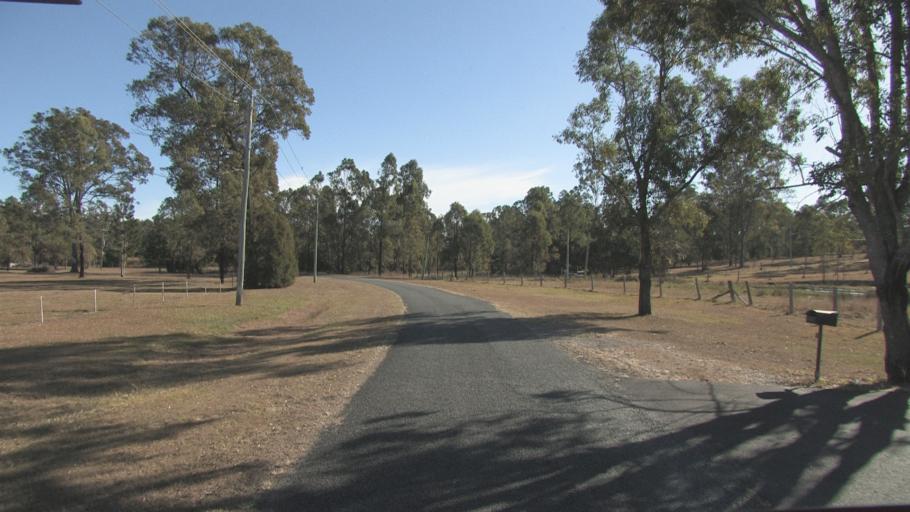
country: AU
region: Queensland
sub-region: Logan
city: Cedar Vale
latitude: -27.8460
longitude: 153.0082
